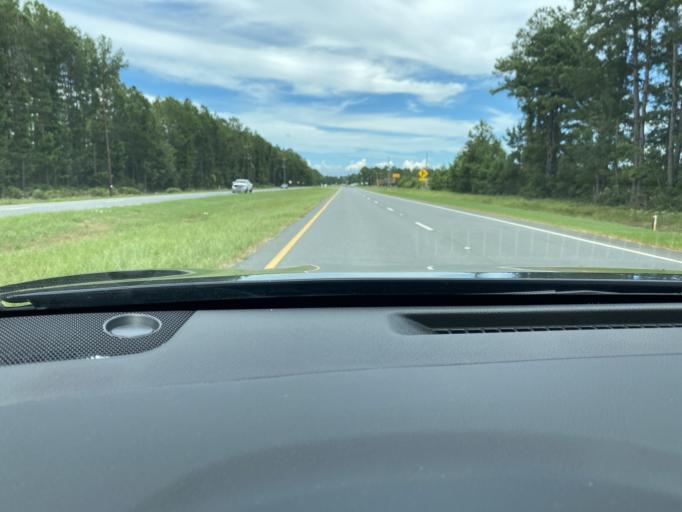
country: US
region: Georgia
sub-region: Brantley County
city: Nahunta
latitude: 31.2000
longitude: -82.0075
